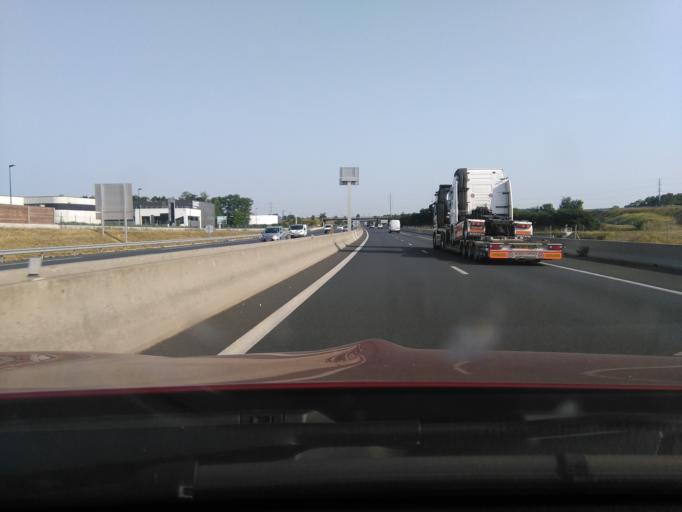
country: FR
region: Rhone-Alpes
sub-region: Departement du Rhone
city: Cailloux-sur-Fontaines
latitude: 45.8665
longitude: 4.9055
